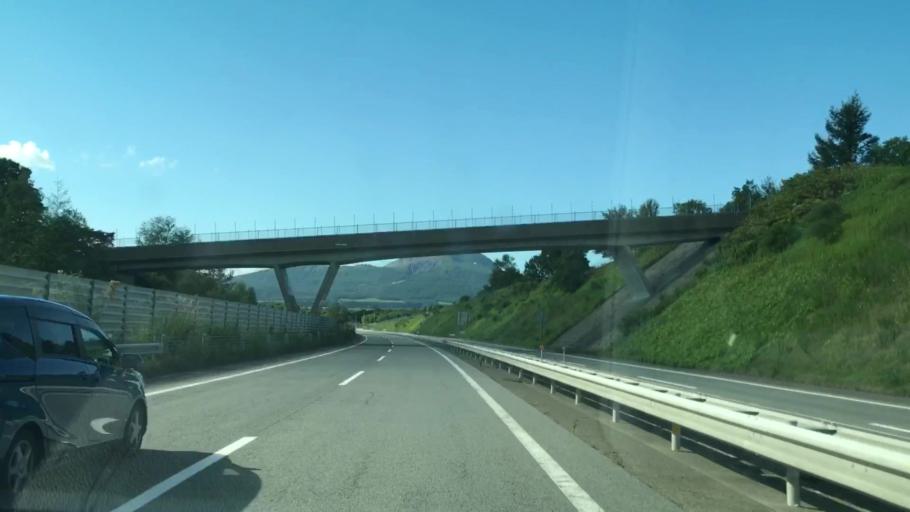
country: JP
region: Hokkaido
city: Date
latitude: 42.4807
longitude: 140.8983
